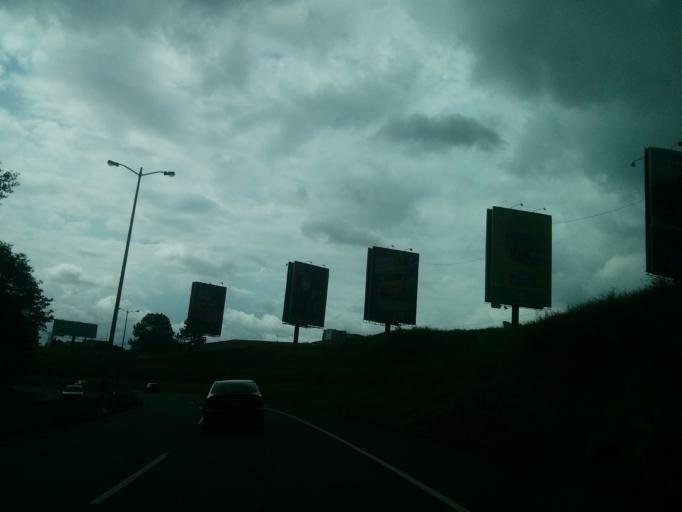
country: CR
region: San Jose
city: San Rafael
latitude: 9.9359
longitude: -84.1133
